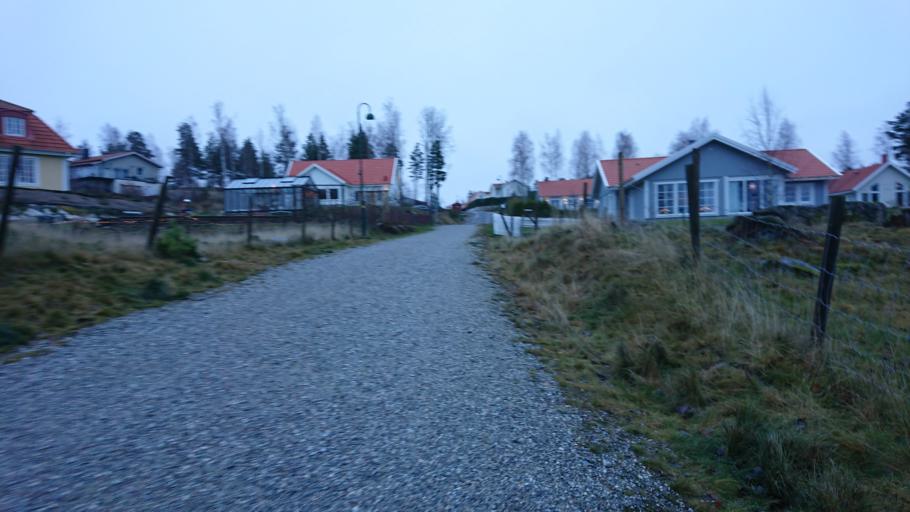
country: SE
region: Soedermanland
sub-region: Strangnas Kommun
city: Stallarholmen
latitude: 59.3661
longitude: 17.1869
